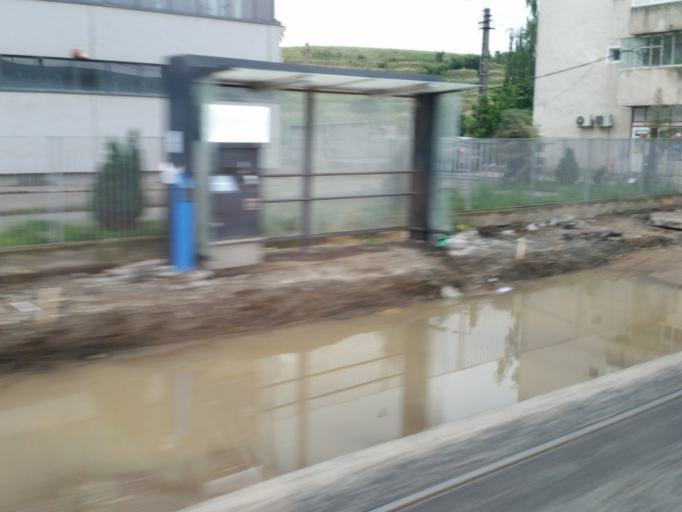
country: RO
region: Cluj
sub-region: Municipiul Cluj-Napoca
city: Cluj-Napoca
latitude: 46.7960
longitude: 23.6344
